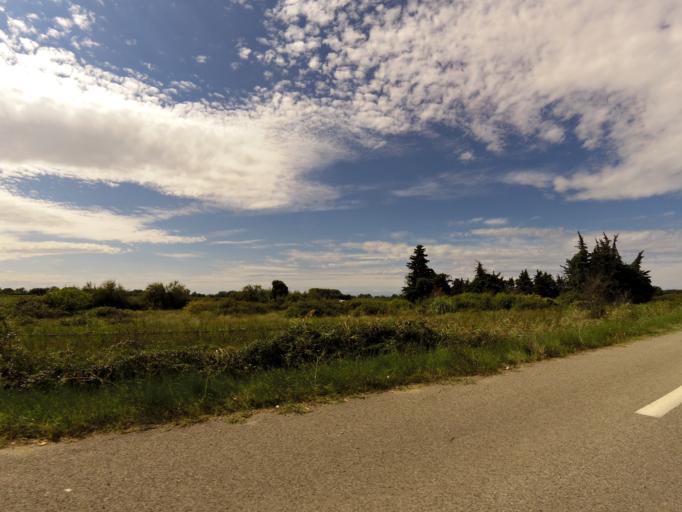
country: FR
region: Languedoc-Roussillon
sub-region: Departement de l'Herault
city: Marsillargues
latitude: 43.6259
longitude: 4.1906
